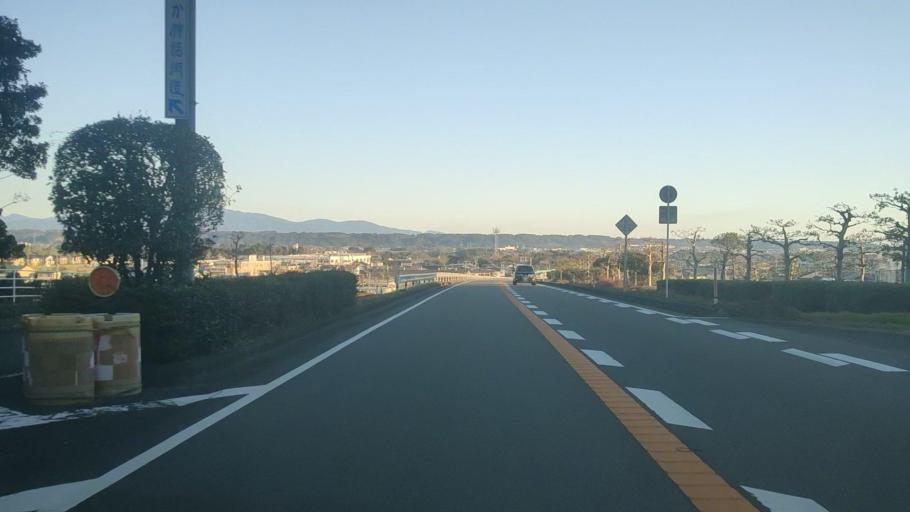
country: JP
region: Miyazaki
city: Tsuma
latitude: 32.0329
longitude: 131.4650
